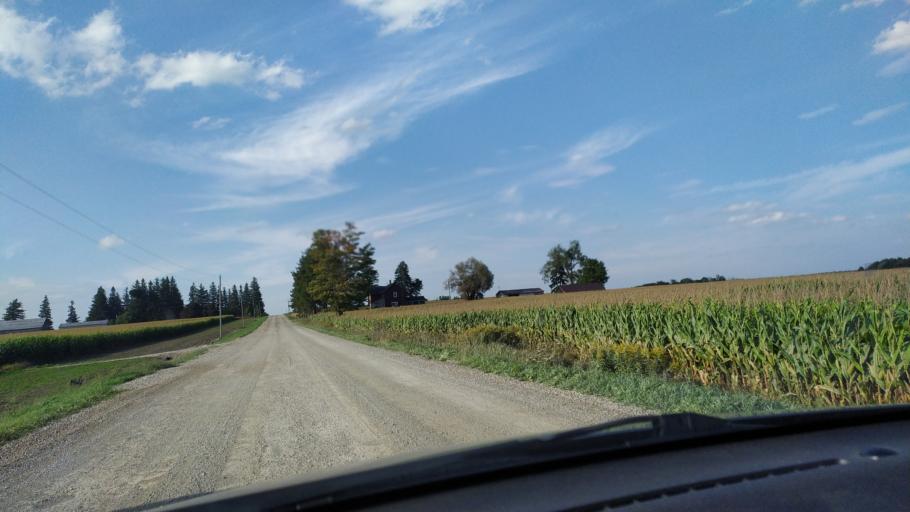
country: CA
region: Ontario
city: Stratford
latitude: 43.2778
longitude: -80.9435
